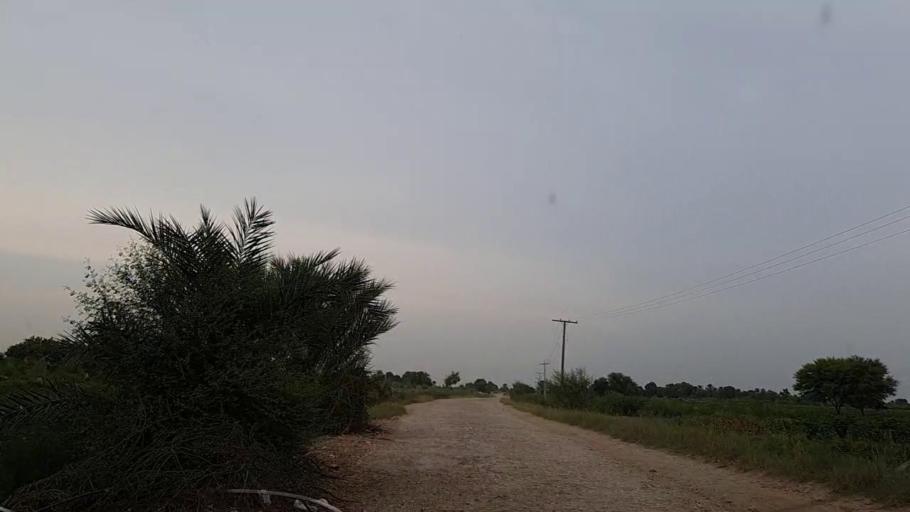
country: PK
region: Sindh
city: Mirpur Mathelo
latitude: 27.8649
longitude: 69.6326
